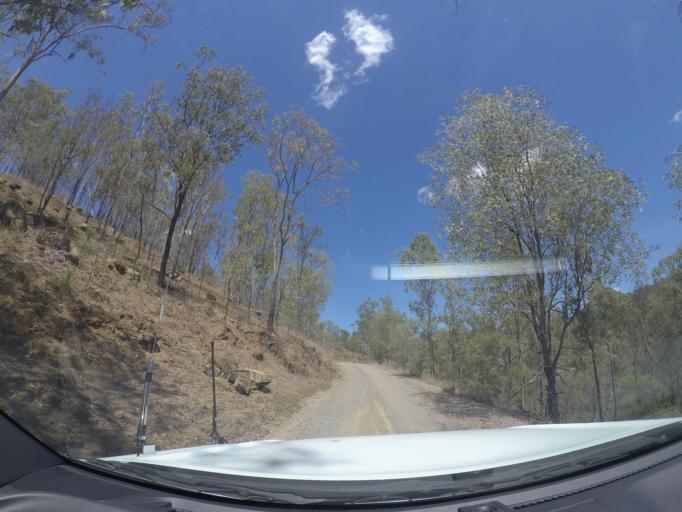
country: AU
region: Queensland
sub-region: Ipswich
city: Springfield Lakes
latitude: -27.8162
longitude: 152.8496
